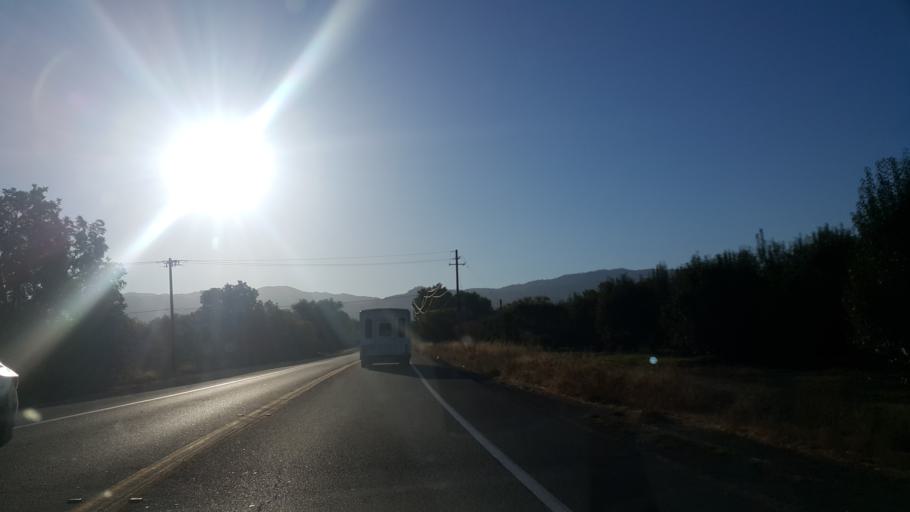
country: US
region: California
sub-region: Mendocino County
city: Ukiah
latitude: 39.1359
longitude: -123.1908
